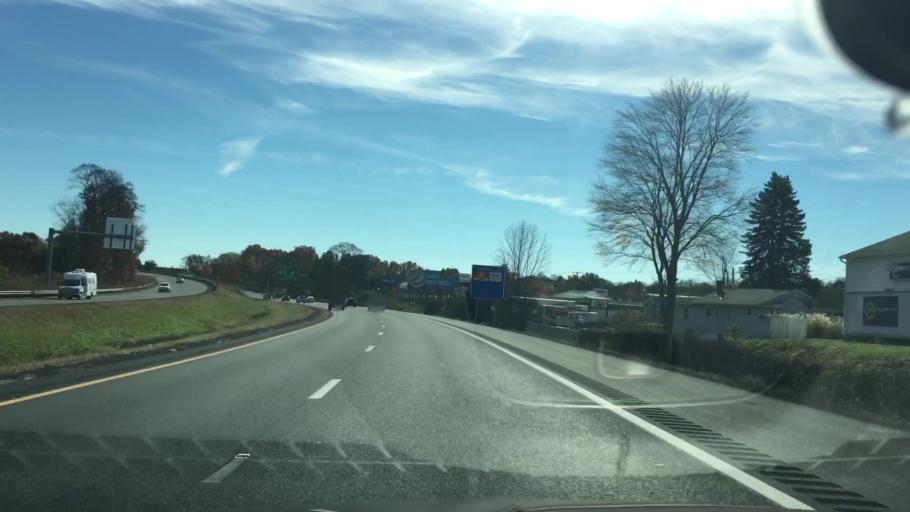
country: US
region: Massachusetts
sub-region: Hampshire County
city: Northampton
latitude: 42.3457
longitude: -72.6426
